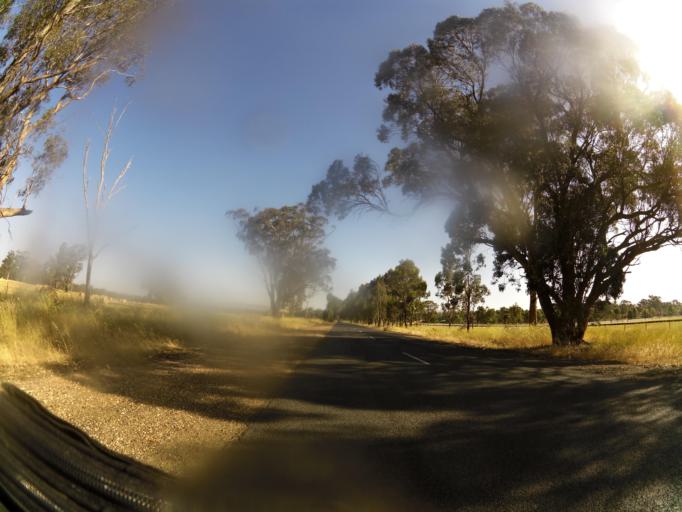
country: AU
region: Victoria
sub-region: Murrindindi
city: Kinglake West
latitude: -36.9828
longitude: 145.1111
